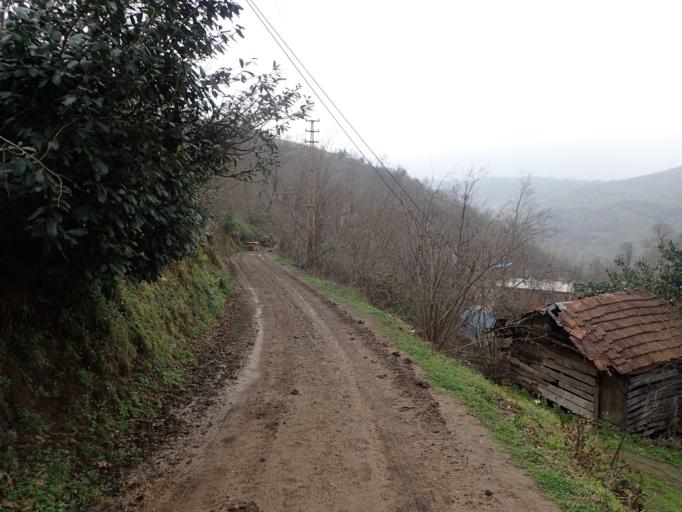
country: TR
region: Ordu
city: Camas
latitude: 40.9222
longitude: 37.5643
